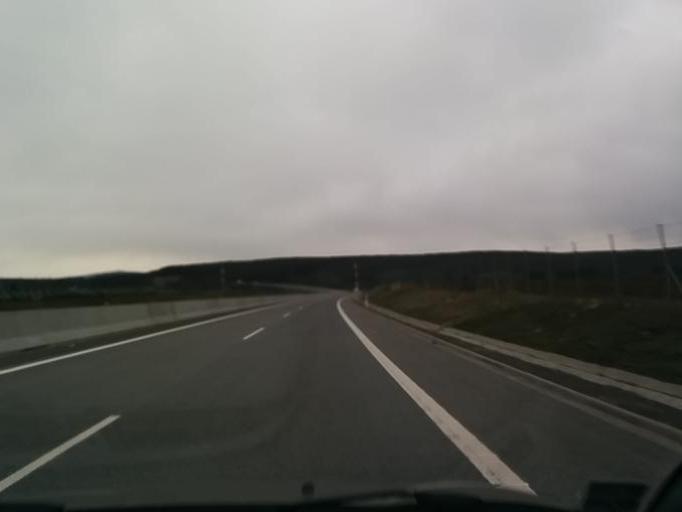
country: SK
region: Nitriansky
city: Zlate Moravce
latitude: 48.3535
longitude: 18.4629
